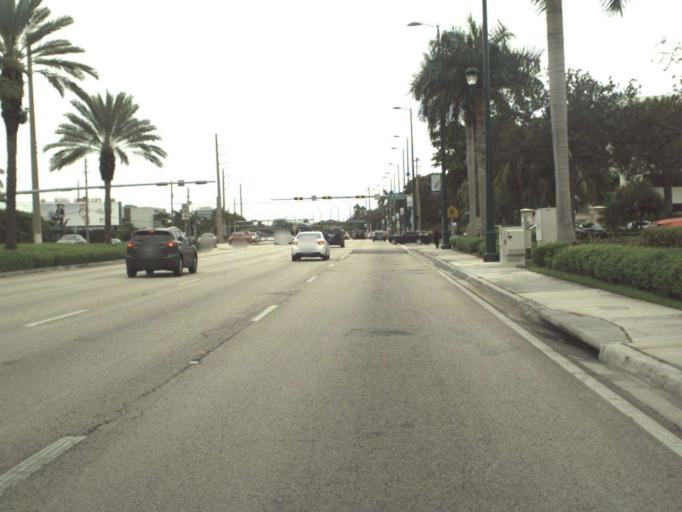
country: US
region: Florida
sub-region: Miami-Dade County
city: Ojus
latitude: 25.9445
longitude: -80.1477
